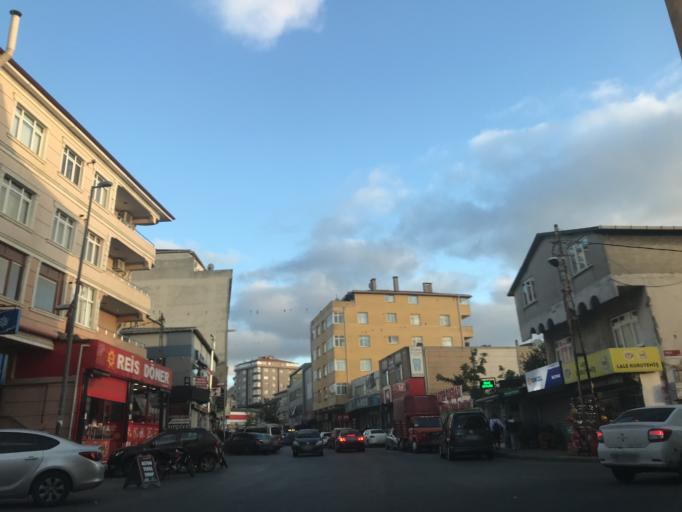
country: TR
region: Istanbul
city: Sisli
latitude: 41.1307
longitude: 29.0413
